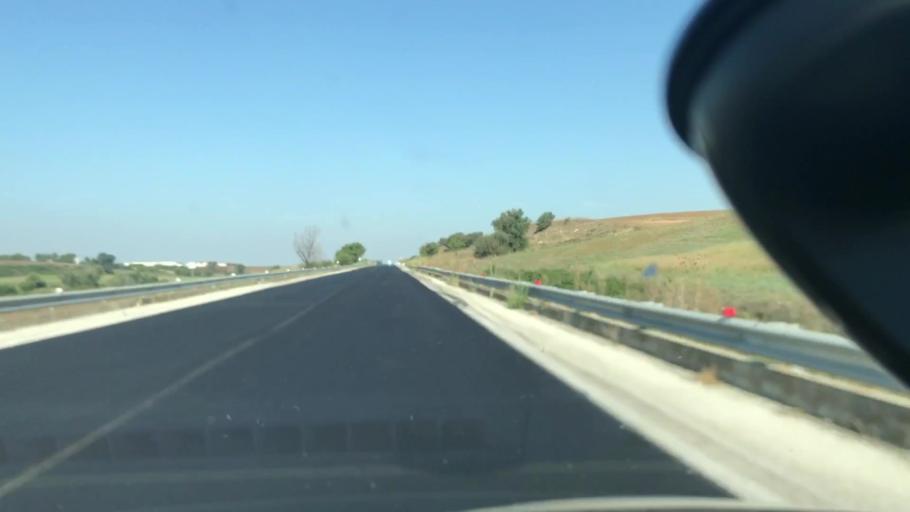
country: IT
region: Apulia
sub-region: Provincia di Barletta - Andria - Trani
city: Spinazzola
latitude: 40.9039
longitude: 16.1157
